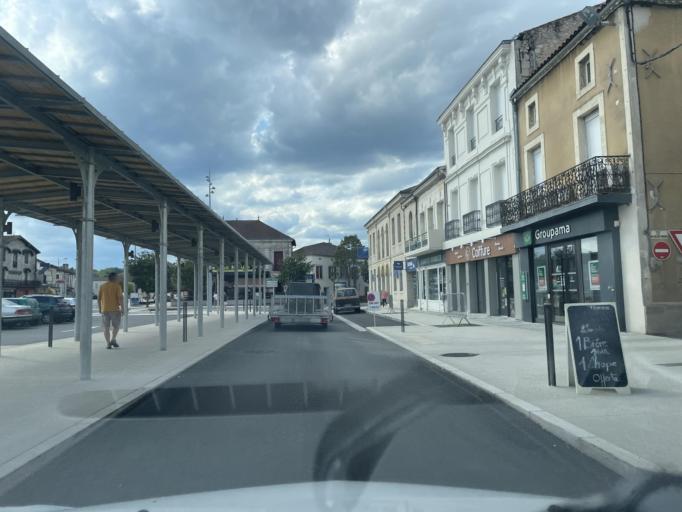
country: FR
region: Aquitaine
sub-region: Departement du Lot-et-Garonne
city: Casteljaloux
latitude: 44.3143
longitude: 0.0858
